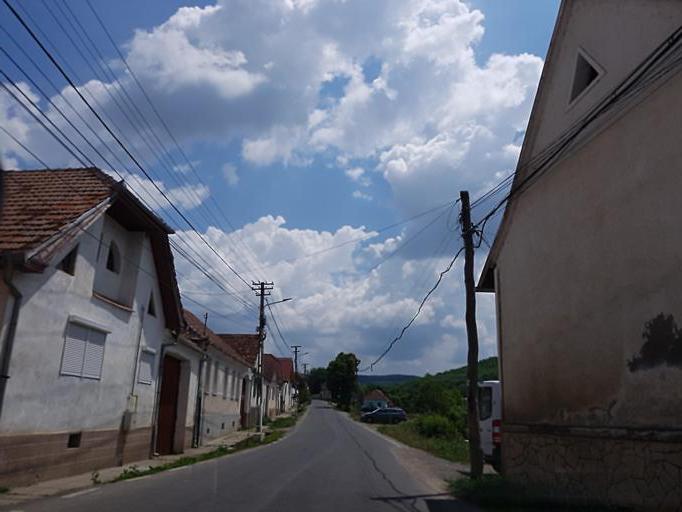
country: RO
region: Sibiu
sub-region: Comuna Seica Mica
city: Seica Mica
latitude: 46.0554
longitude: 24.1277
